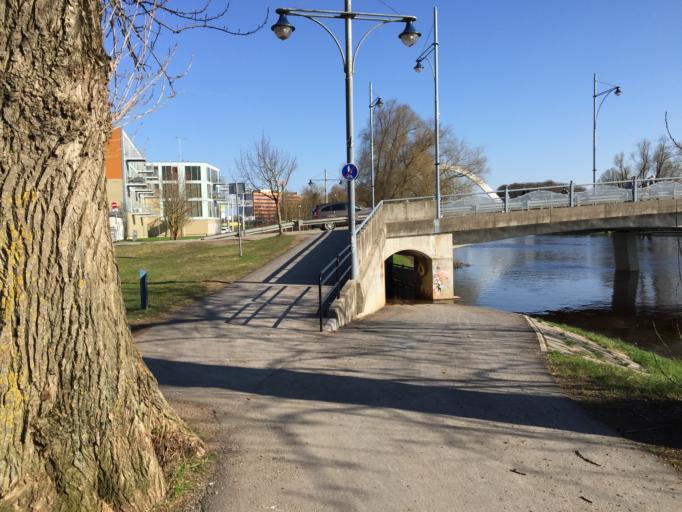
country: EE
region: Tartu
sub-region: Tartu linn
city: Tartu
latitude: 58.3870
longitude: 26.7222
